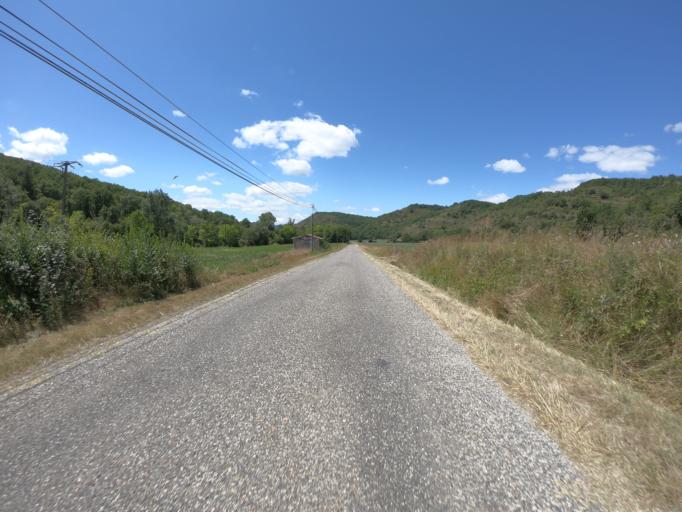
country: FR
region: Midi-Pyrenees
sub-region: Departement de l'Ariege
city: Mirepoix
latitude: 43.0519
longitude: 1.8120
